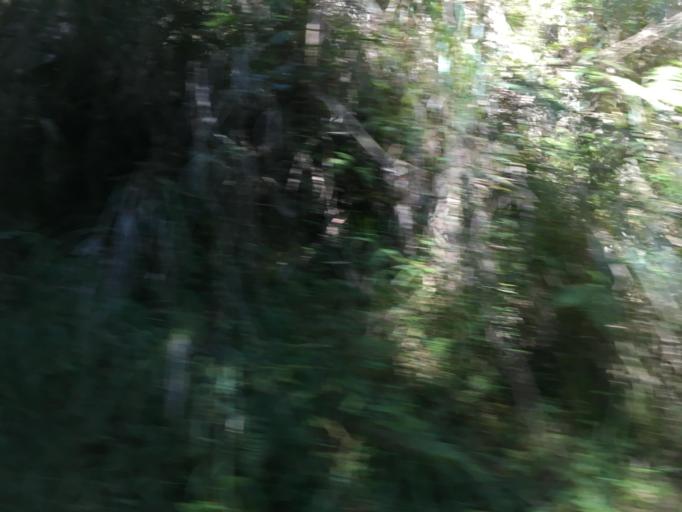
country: TW
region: Taiwan
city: Daxi
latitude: 24.5727
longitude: 121.4190
